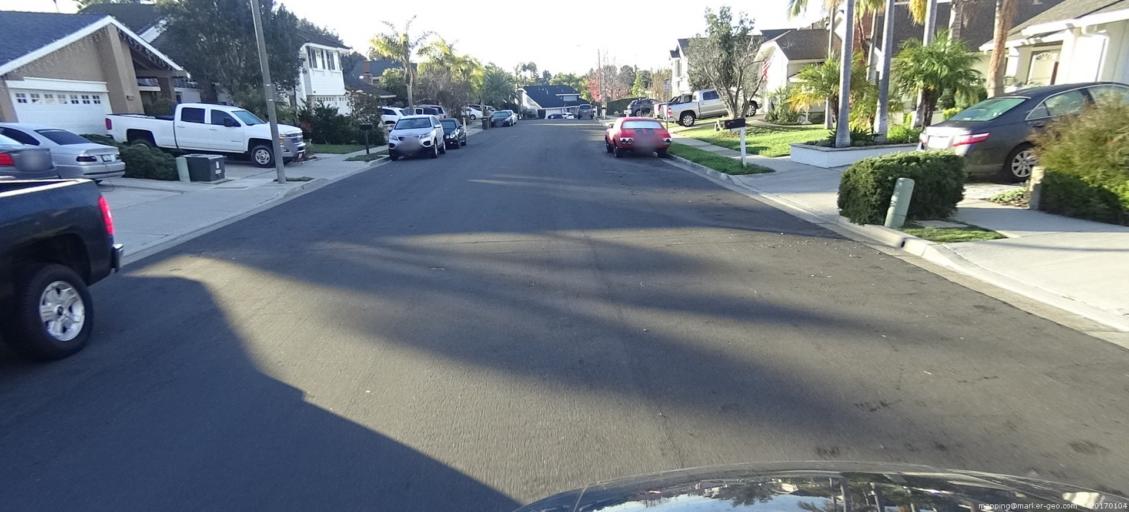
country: US
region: California
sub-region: Orange County
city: Dana Point
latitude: 33.4832
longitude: -117.6986
